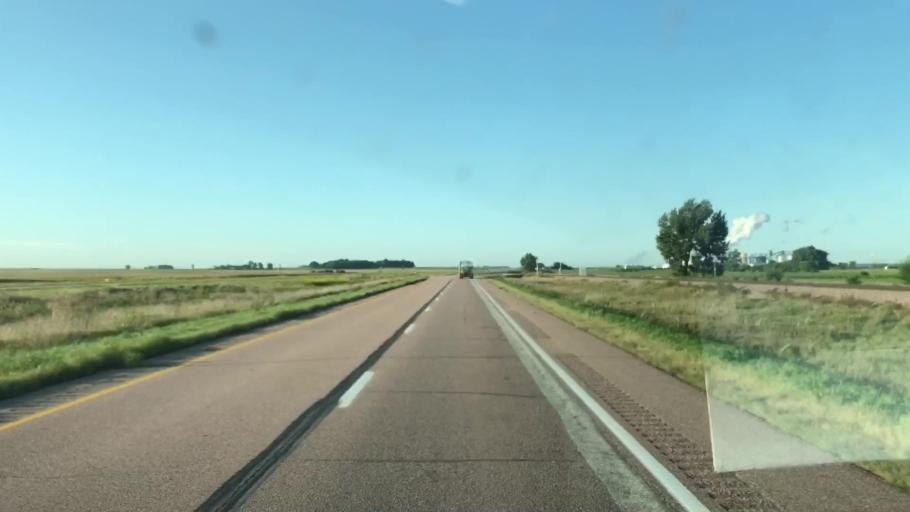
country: US
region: Iowa
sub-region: Osceola County
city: Sibley
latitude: 43.2899
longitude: -95.7974
